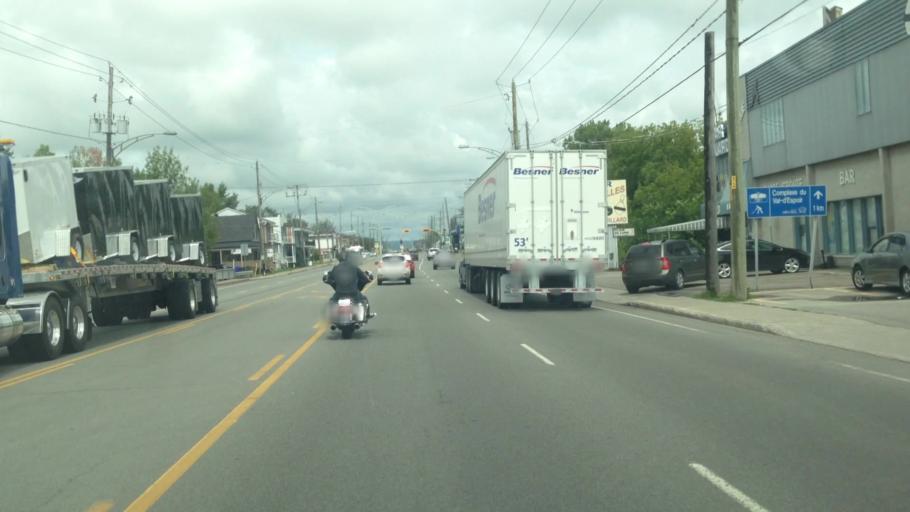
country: CA
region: Quebec
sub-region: Laurentides
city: Blainville
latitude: 45.7035
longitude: -73.9266
